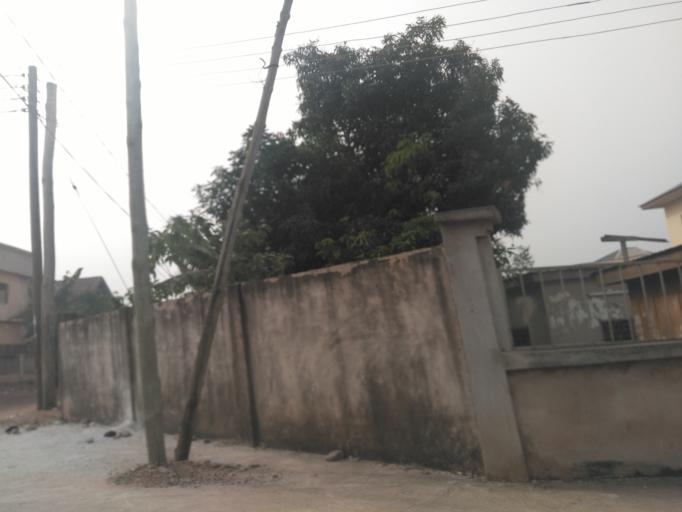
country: GH
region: Ashanti
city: Kumasi
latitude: 6.6662
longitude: -1.6171
